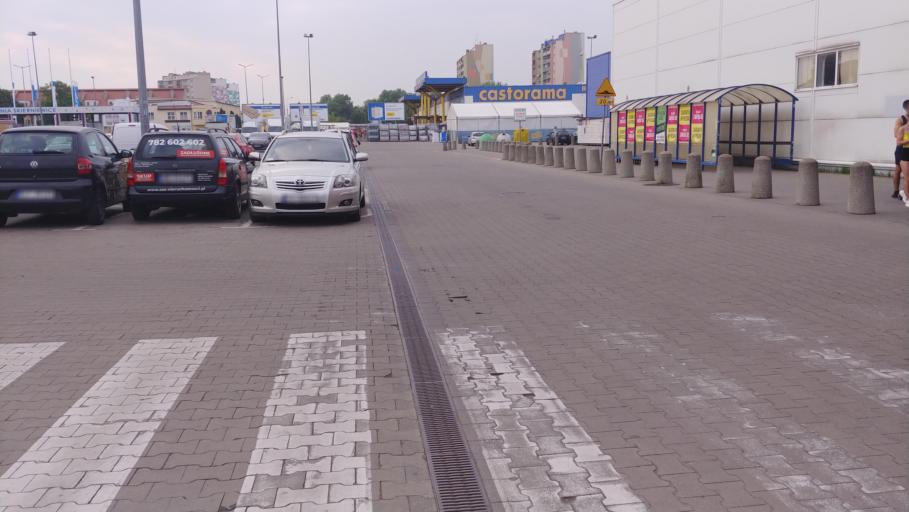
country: PL
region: Lodz Voivodeship
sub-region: Skierniewice
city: Skierniewice
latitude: 51.9724
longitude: 20.1464
